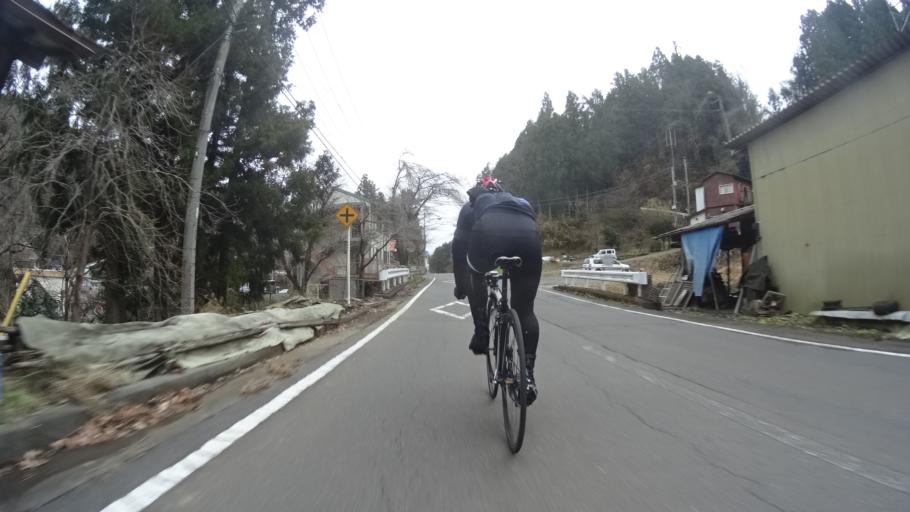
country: JP
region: Yamanashi
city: Uenohara
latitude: 35.6362
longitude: 139.0632
